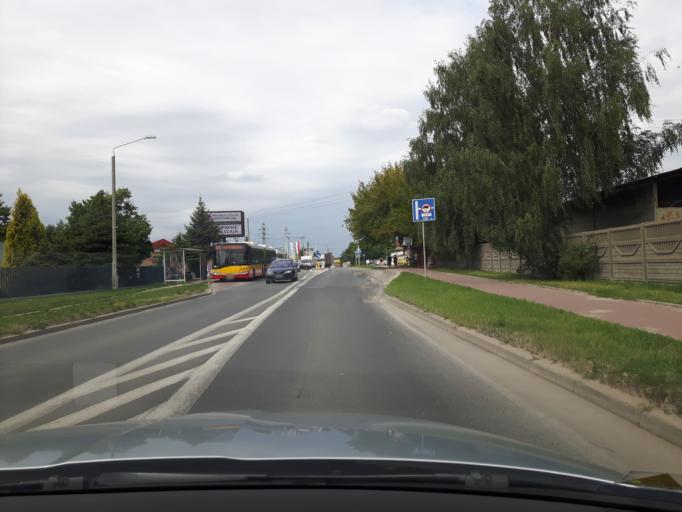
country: PL
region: Masovian Voivodeship
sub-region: Powiat wolominski
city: Zabki
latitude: 52.2768
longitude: 21.1160
